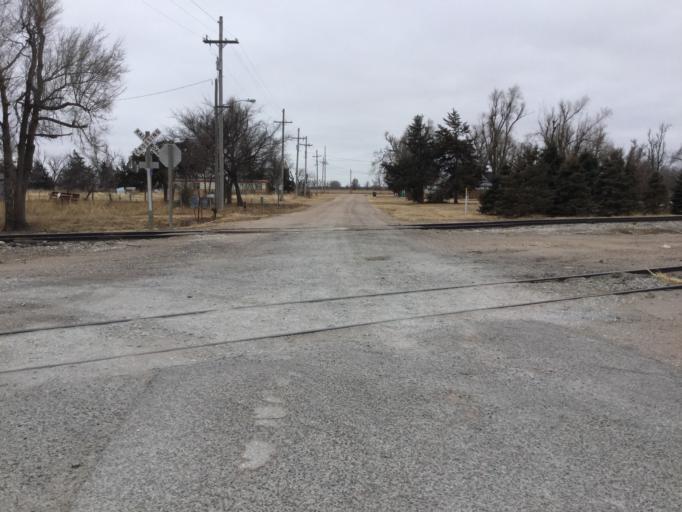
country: US
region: Kansas
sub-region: Pawnee County
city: Larned
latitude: 38.2632
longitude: -98.9832
